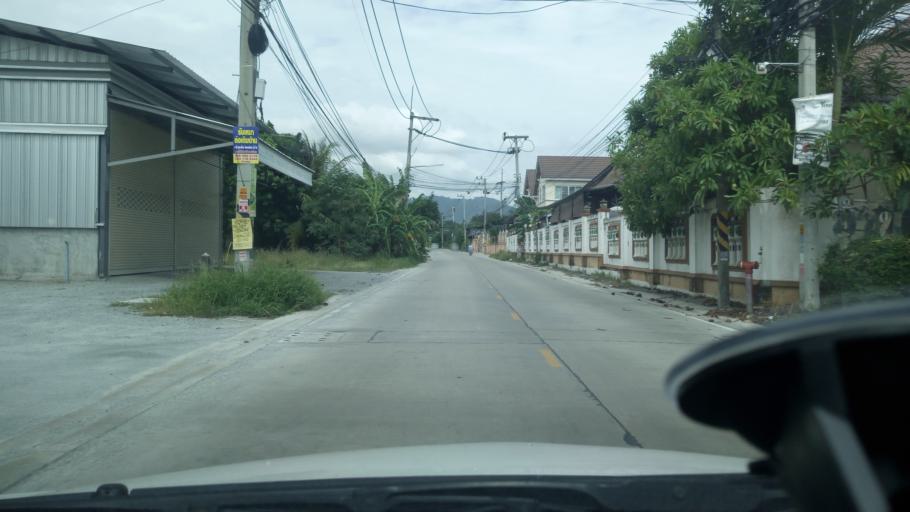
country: TH
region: Chon Buri
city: Chon Buri
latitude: 13.2947
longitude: 100.9624
